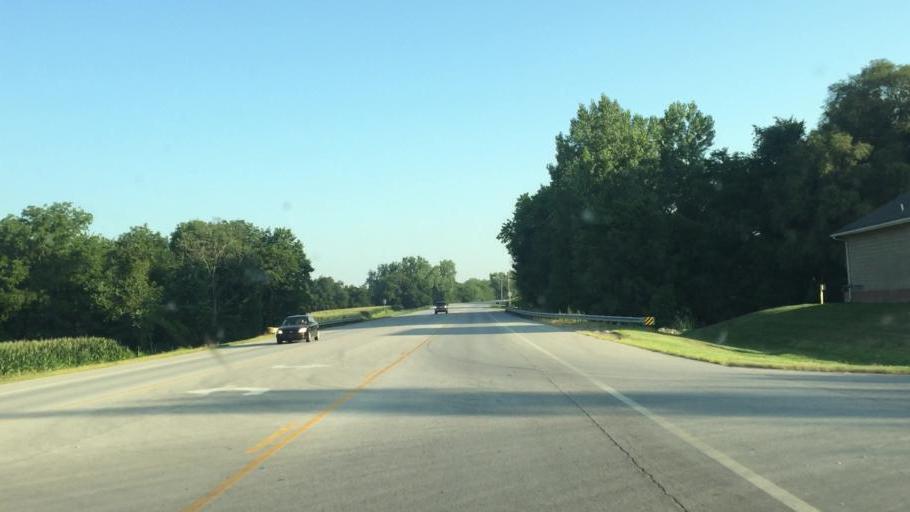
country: US
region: Kansas
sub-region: Doniphan County
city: Wathena
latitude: 39.7665
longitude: -94.9560
